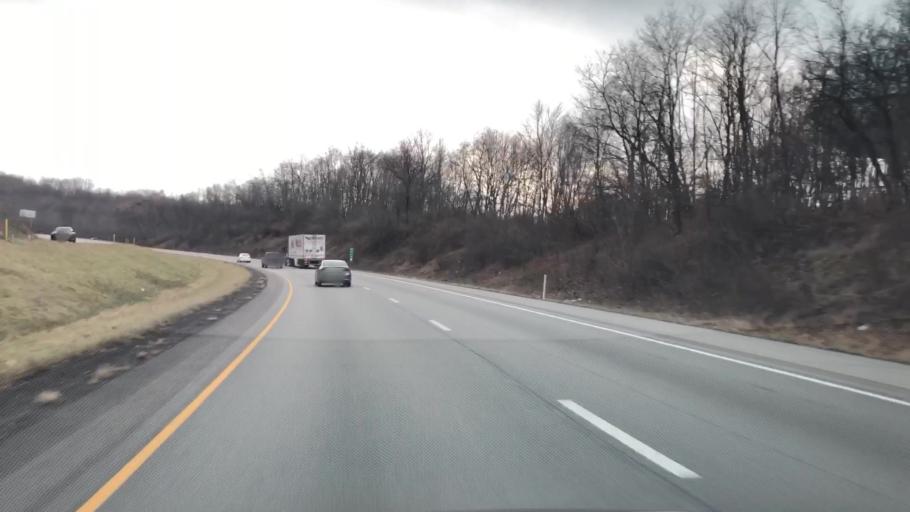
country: US
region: Pennsylvania
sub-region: Butler County
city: Zelienople
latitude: 40.7924
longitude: -80.1246
